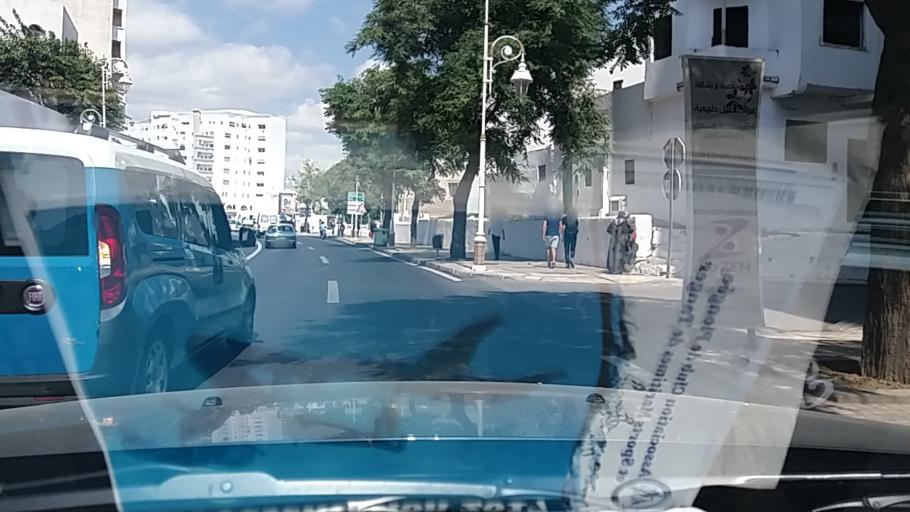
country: MA
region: Tanger-Tetouan
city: Tetouan
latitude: 35.5701
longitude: -5.3596
